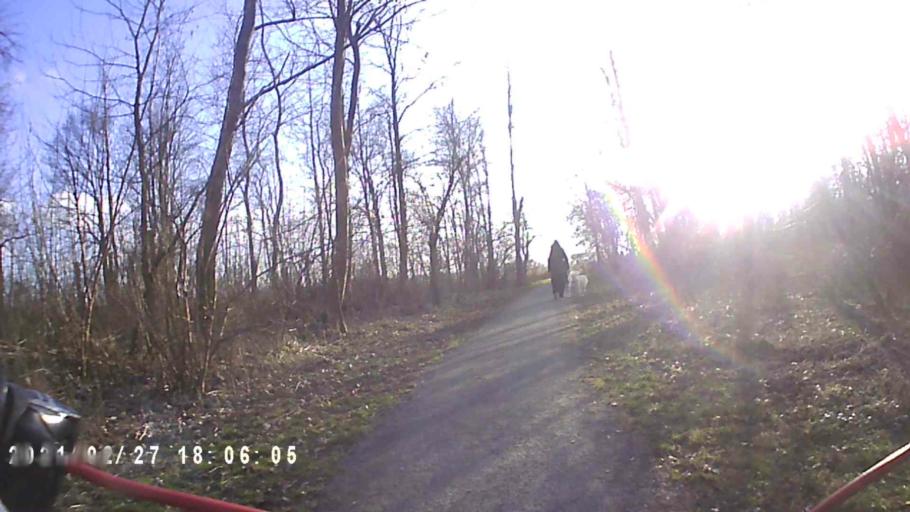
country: NL
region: Groningen
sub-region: Gemeente Bedum
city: Bedum
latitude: 53.2938
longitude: 6.6111
